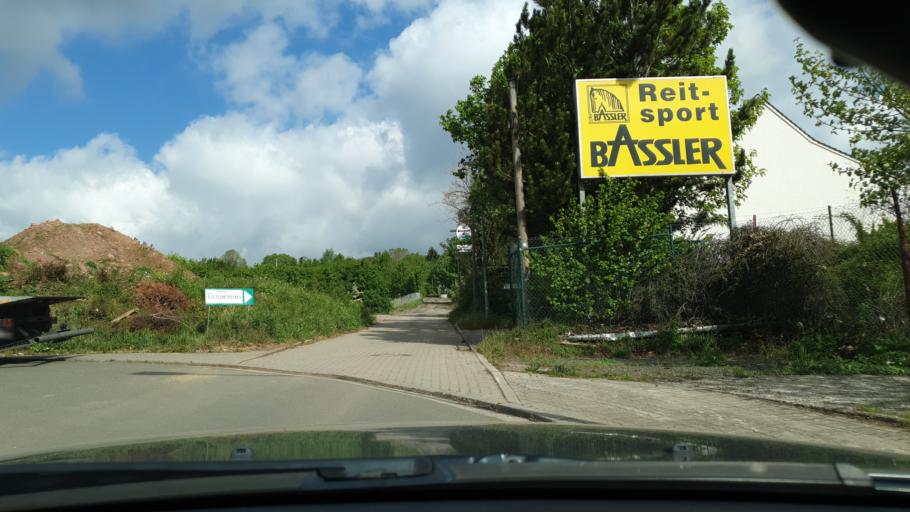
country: DE
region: Rheinland-Pfalz
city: Kaiserslautern
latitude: 49.4561
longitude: 7.7868
